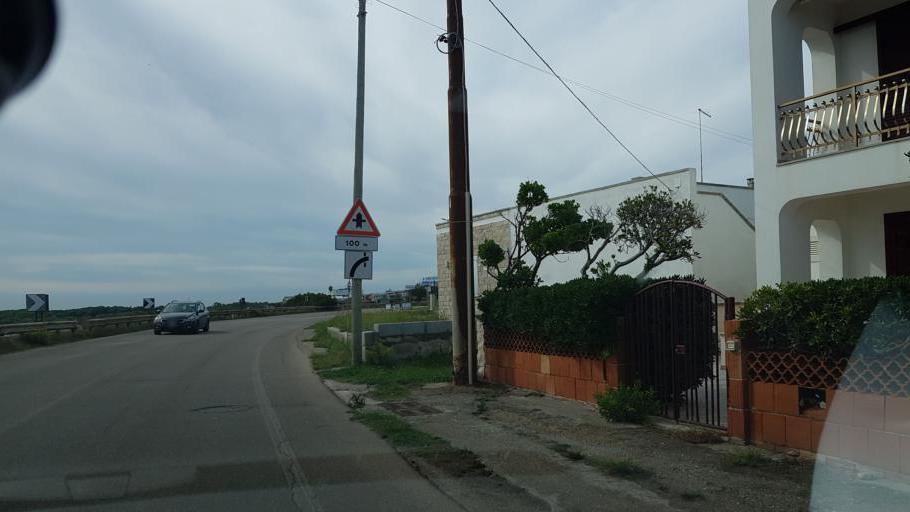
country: IT
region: Apulia
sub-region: Provincia di Lecce
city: Borgagne
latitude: 40.2797
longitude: 18.4314
